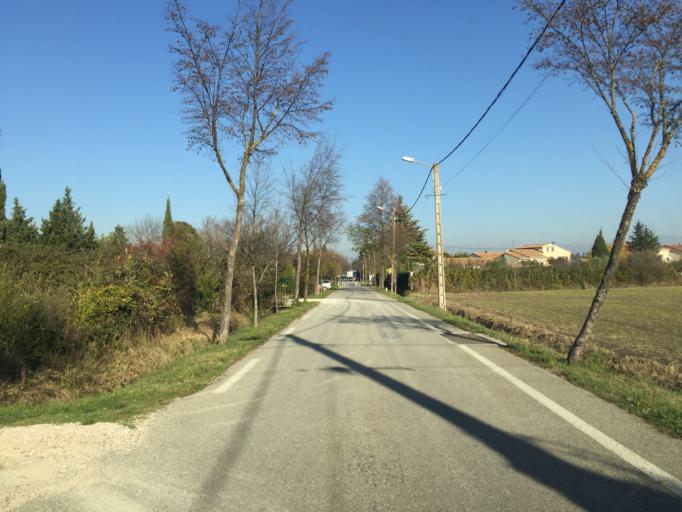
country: FR
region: Provence-Alpes-Cote d'Azur
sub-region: Departement du Vaucluse
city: Entraigues-sur-la-Sorgue
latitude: 44.0069
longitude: 4.9326
